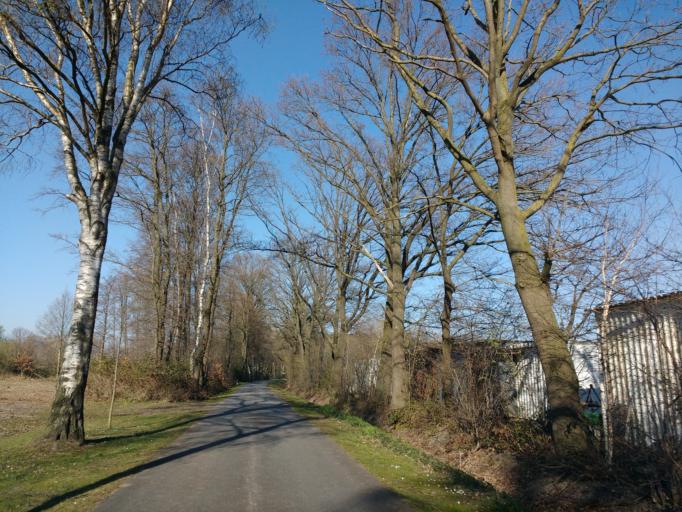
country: DE
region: North Rhine-Westphalia
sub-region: Regierungsbezirk Detmold
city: Delbruck
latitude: 51.7189
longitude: 8.5169
